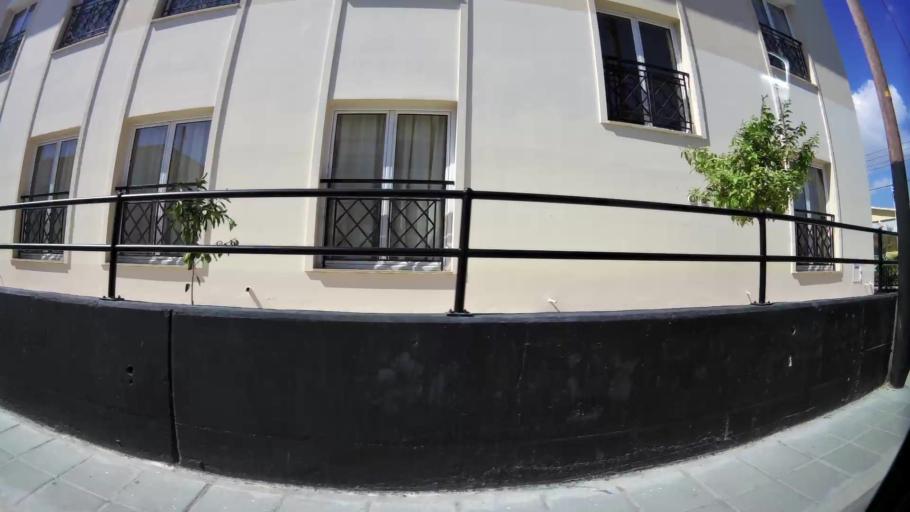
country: CY
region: Larnaka
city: Larnaca
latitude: 34.9109
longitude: 33.6313
